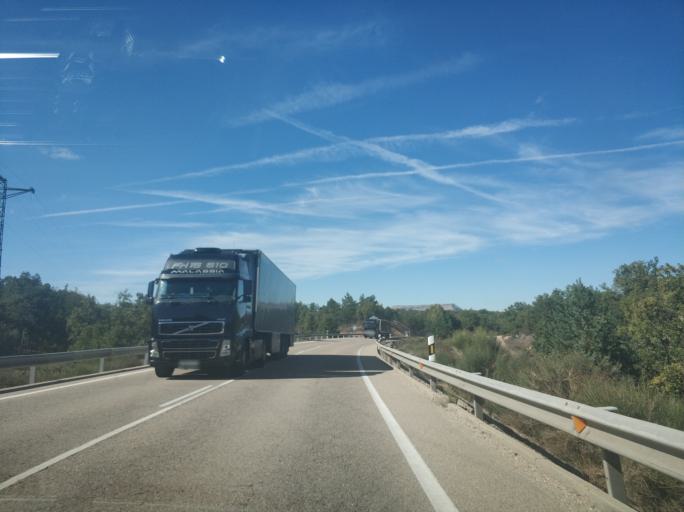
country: ES
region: Castille and Leon
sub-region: Provincia de Burgos
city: Pinilla de los Barruecos
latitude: 41.9148
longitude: -3.2782
